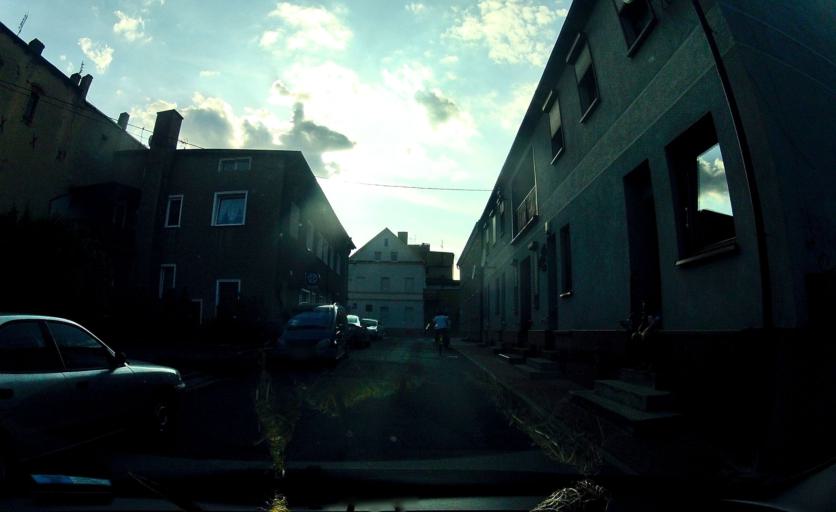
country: PL
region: Opole Voivodeship
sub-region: Powiat oleski
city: Gorzow Slaski
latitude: 51.0283
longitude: 18.4237
